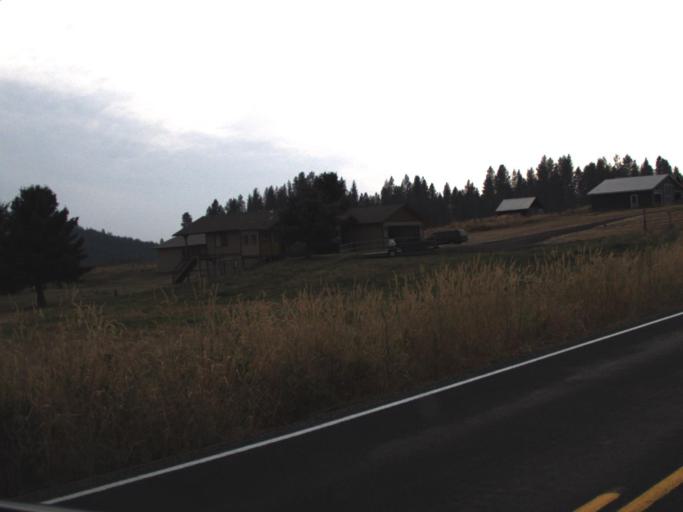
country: US
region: Washington
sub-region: Spokane County
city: Trentwood
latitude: 47.8022
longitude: -117.2267
